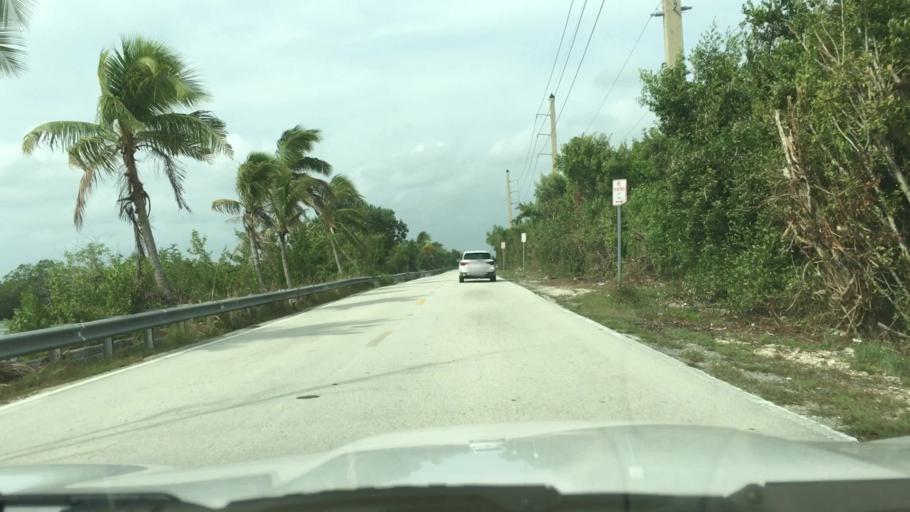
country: US
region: Florida
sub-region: Monroe County
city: North Key Largo
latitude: 25.2954
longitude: -80.3841
